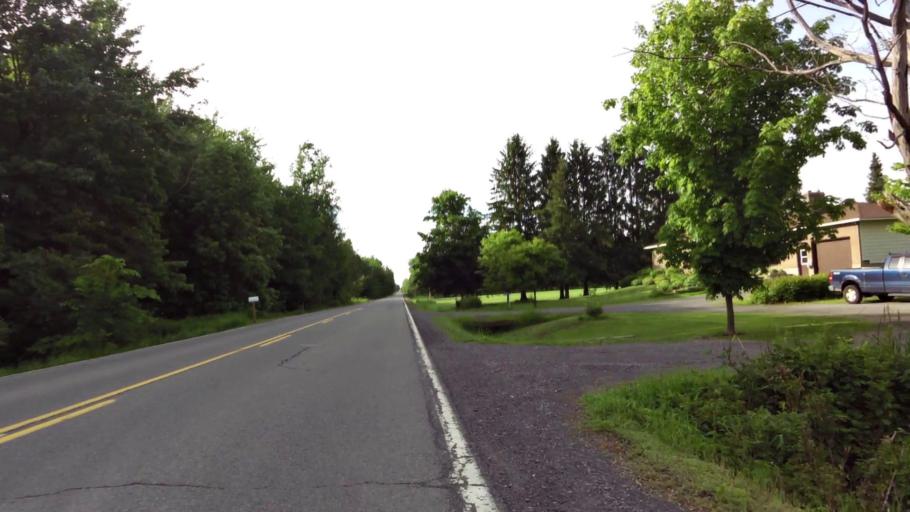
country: CA
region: Ontario
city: Ottawa
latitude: 45.2001
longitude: -75.5913
